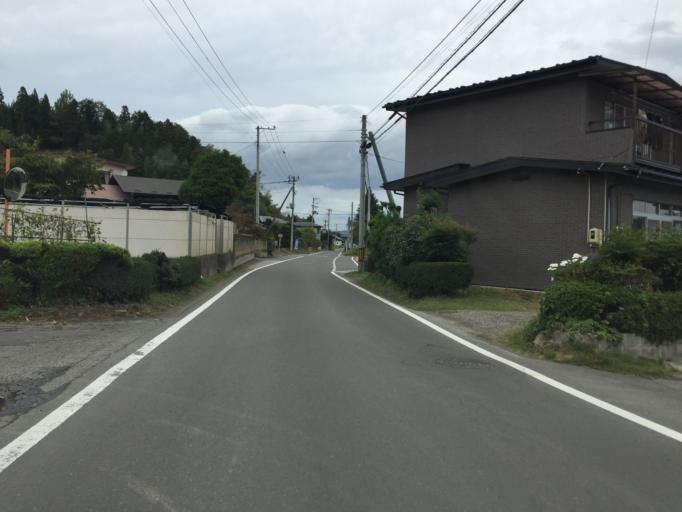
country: JP
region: Miyagi
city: Marumori
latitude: 37.9052
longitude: 140.7590
